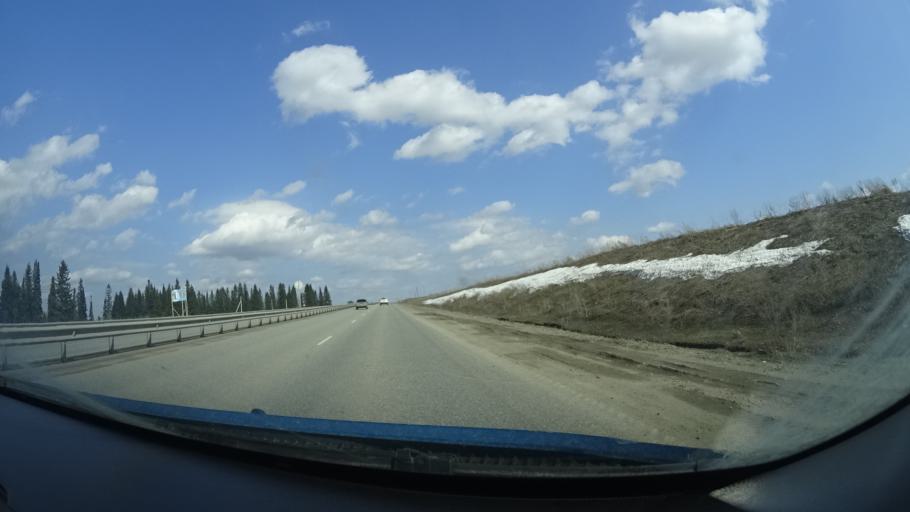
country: RU
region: Perm
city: Kultayevo
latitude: 57.8643
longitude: 55.8797
